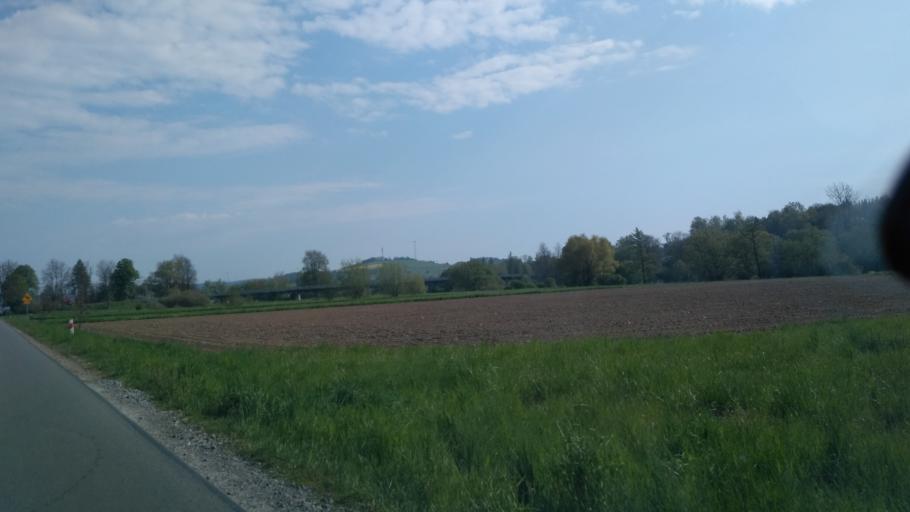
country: PL
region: Subcarpathian Voivodeship
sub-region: Powiat rzeszowski
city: Dynow
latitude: 49.7988
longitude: 22.2408
